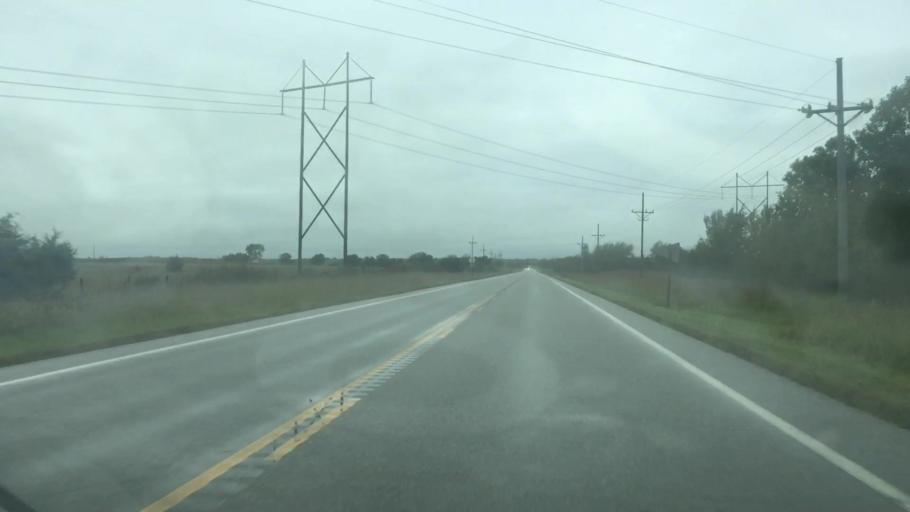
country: US
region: Kansas
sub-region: Anderson County
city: Garnett
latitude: 38.3351
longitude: -95.1706
